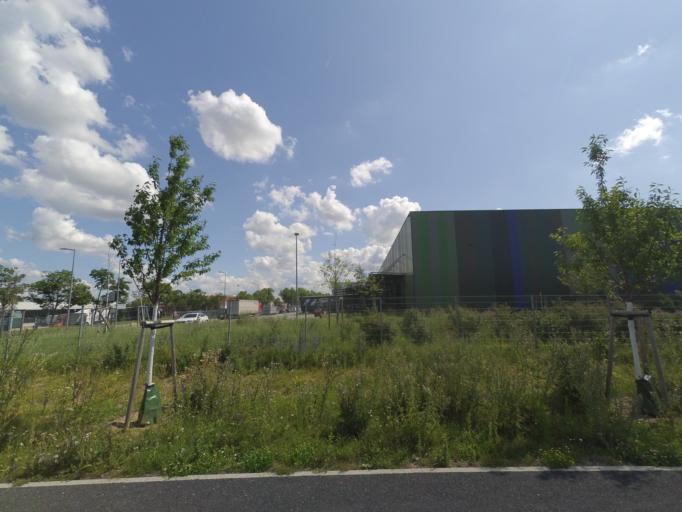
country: DE
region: Hesse
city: Viernheim
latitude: 49.5156
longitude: 8.5560
